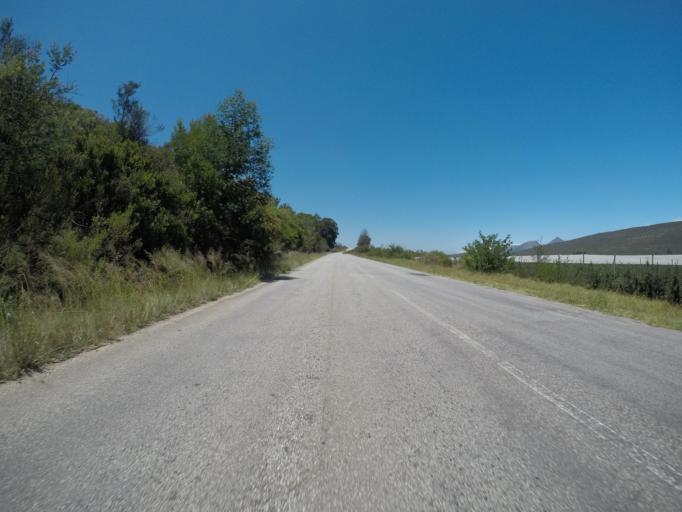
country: ZA
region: Western Cape
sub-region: Eden District Municipality
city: Plettenberg Bay
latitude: -33.8139
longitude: 23.7800
